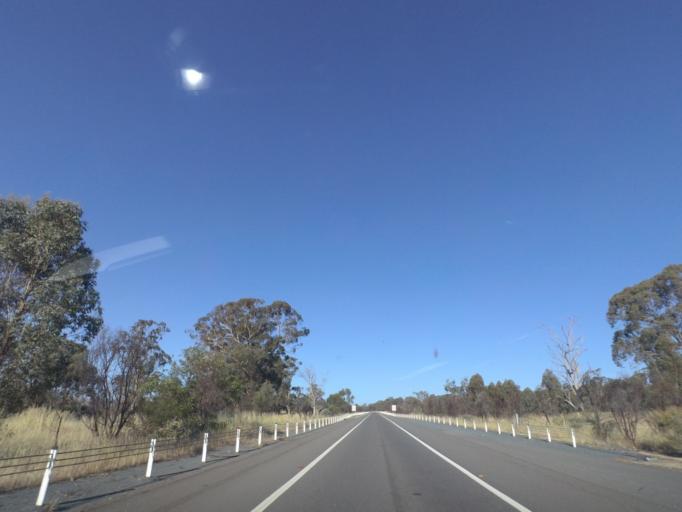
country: AU
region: New South Wales
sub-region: Wagga Wagga
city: Forest Hill
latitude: -35.2593
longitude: 147.7484
